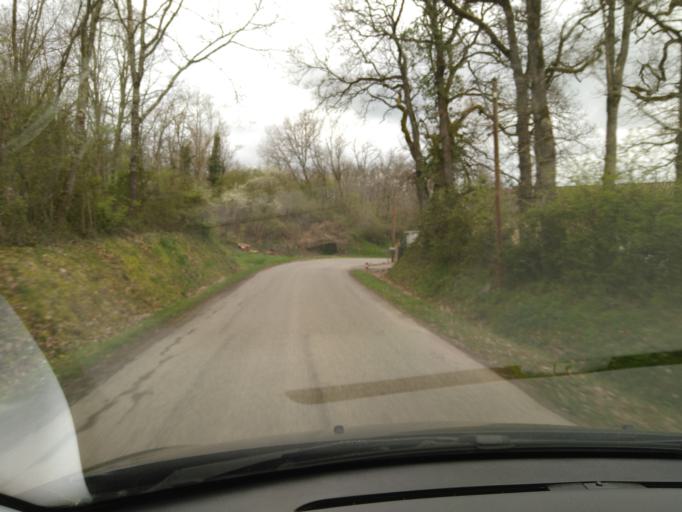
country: FR
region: Midi-Pyrenees
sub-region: Departement du Tarn-et-Garonne
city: Saint-Porquier
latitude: 43.9600
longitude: 1.1308
